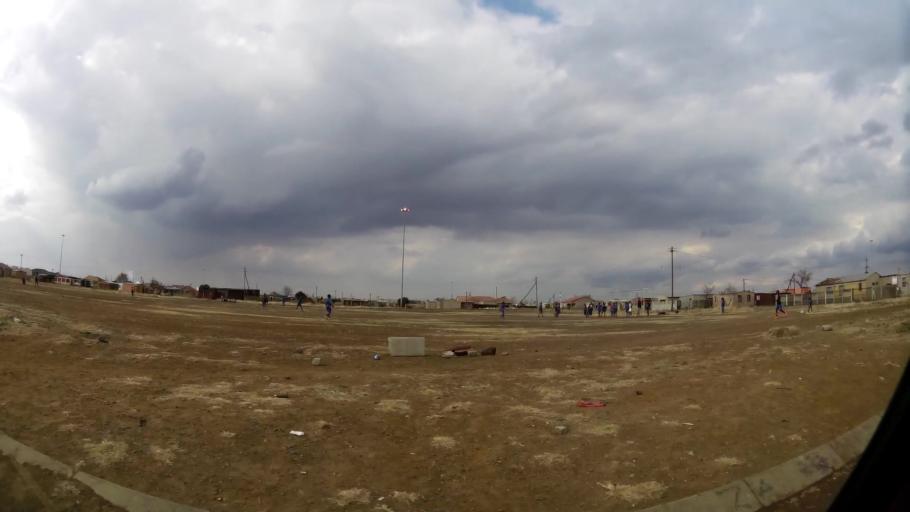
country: ZA
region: Gauteng
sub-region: Sedibeng District Municipality
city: Vanderbijlpark
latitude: -26.6870
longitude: 27.7798
